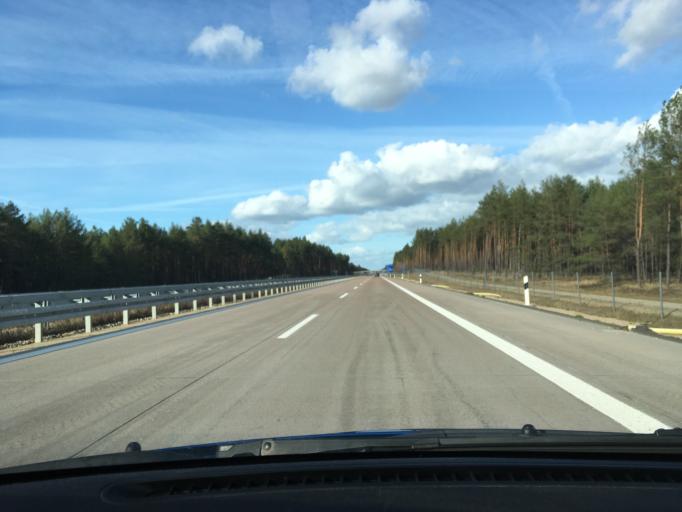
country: DE
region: Mecklenburg-Vorpommern
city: Grabow
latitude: 53.2870
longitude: 11.5269
